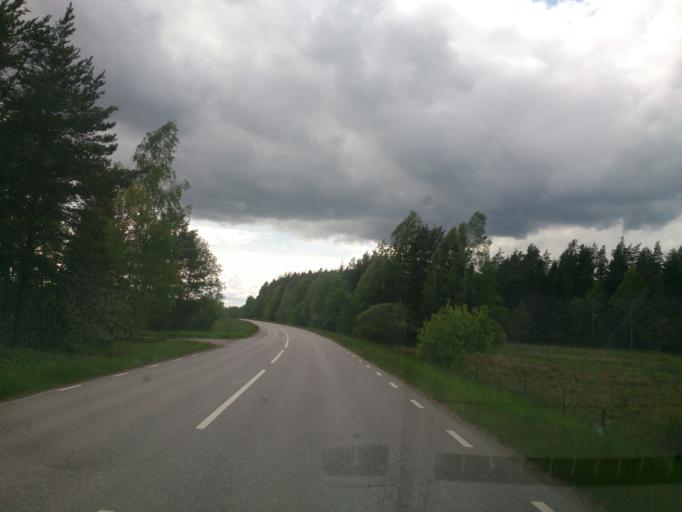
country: SE
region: OEstergoetland
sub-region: Linkopings Kommun
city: Linghem
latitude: 58.4052
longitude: 15.8295
